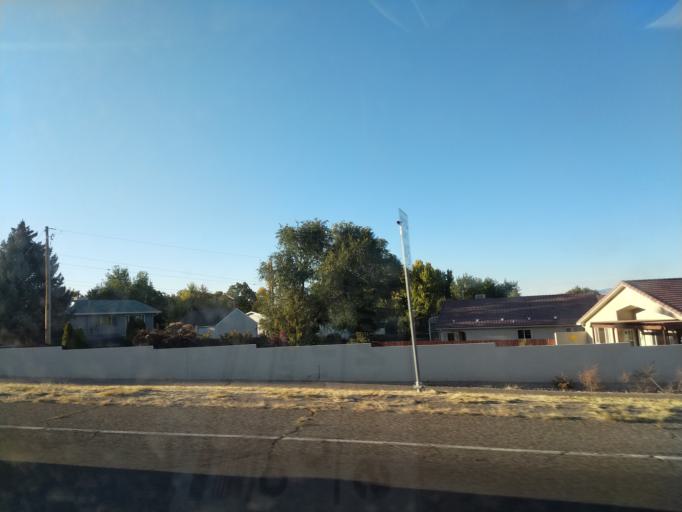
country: US
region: Colorado
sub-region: Mesa County
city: Grand Junction
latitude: 39.0645
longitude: -108.5912
